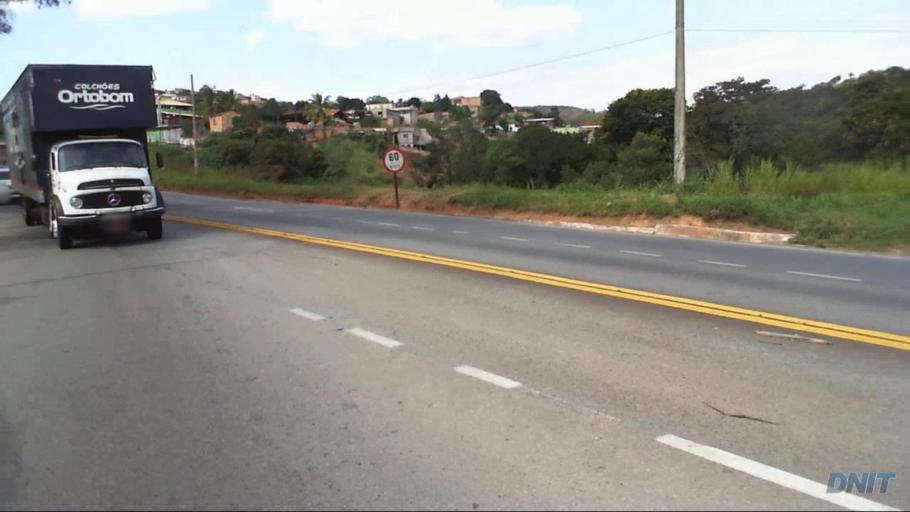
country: BR
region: Minas Gerais
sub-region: Santa Luzia
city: Santa Luzia
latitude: -19.8270
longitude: -43.8373
